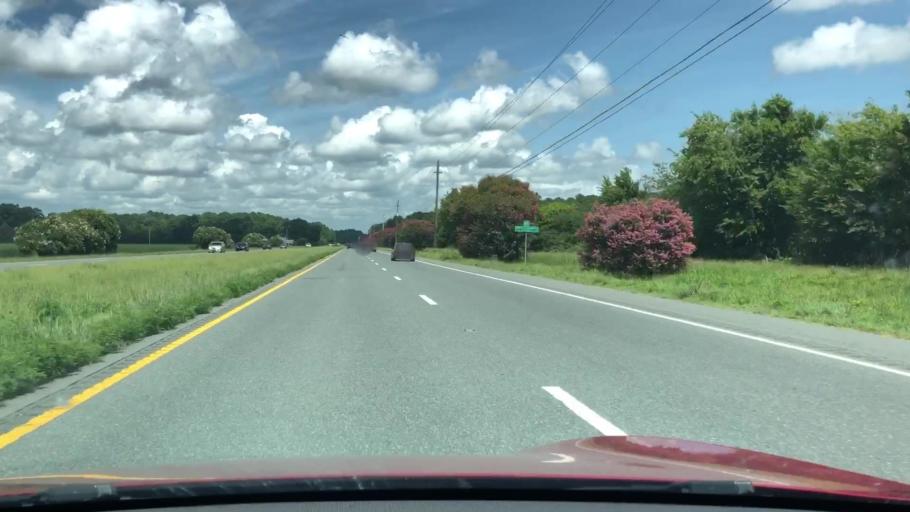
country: US
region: Virginia
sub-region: Northampton County
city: Eastville
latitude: 37.4088
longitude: -75.9005
